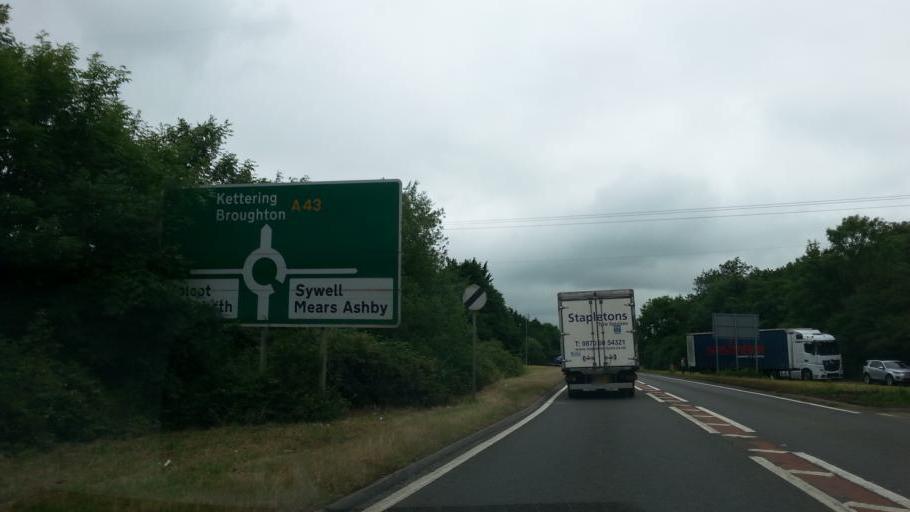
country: GB
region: England
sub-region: Northamptonshire
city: Earls Barton
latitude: 52.3083
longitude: -0.8172
